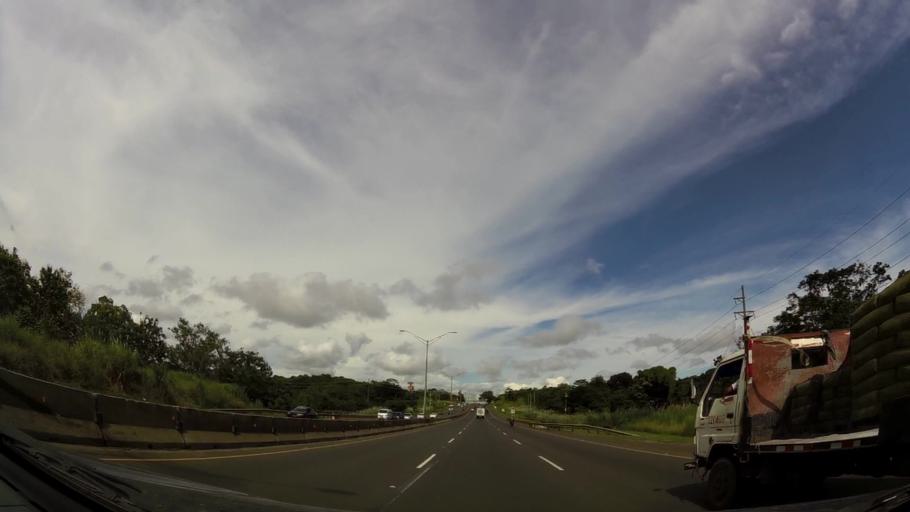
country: PA
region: Panama
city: La Chorrera
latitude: 8.8862
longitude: -79.7546
